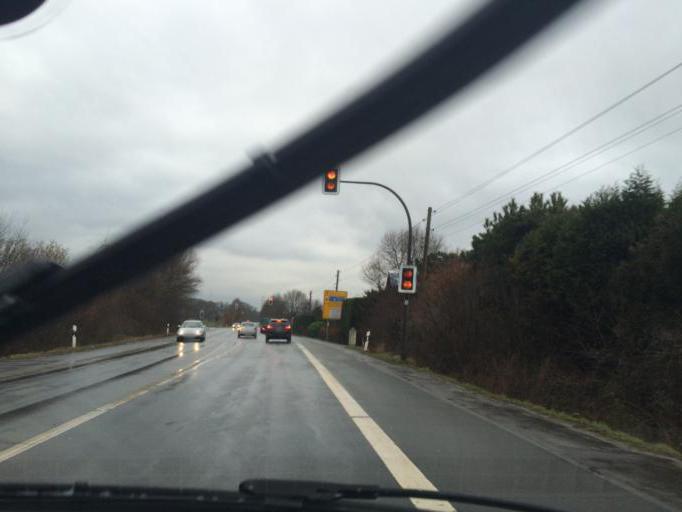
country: DE
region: North Rhine-Westphalia
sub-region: Regierungsbezirk Munster
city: Gladbeck
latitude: 51.6096
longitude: 6.9591
